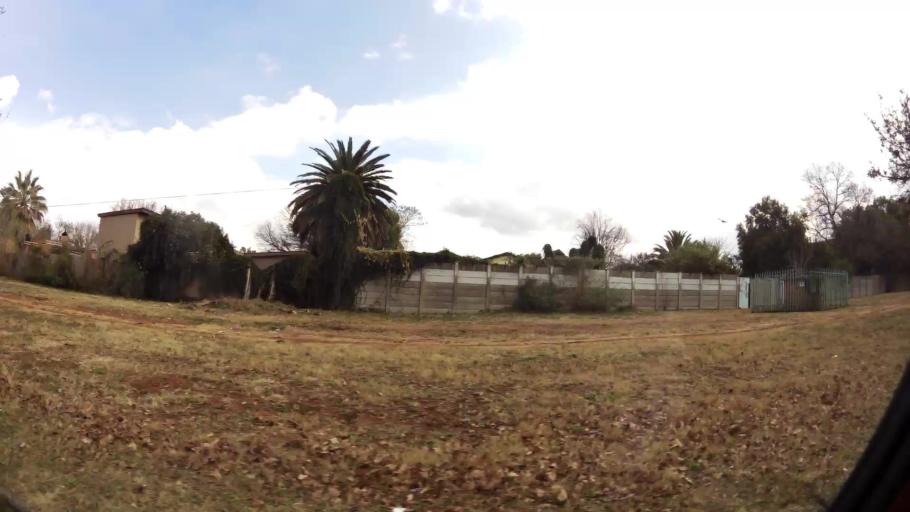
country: ZA
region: Gauteng
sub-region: Sedibeng District Municipality
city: Vanderbijlpark
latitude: -26.7280
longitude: 27.8372
